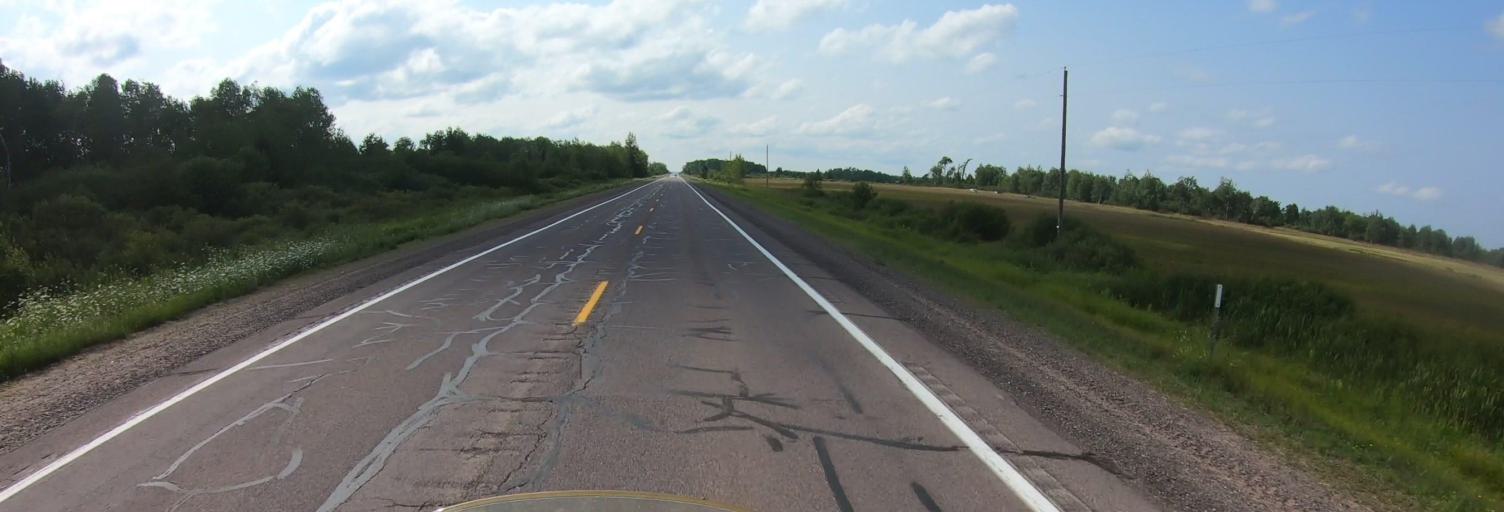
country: US
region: Michigan
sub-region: Ontonagon County
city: Ontonagon
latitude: 46.5503
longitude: -89.3703
